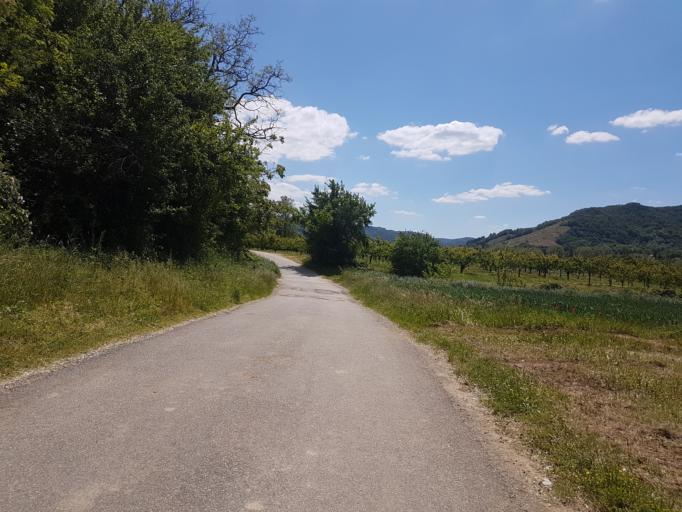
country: FR
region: Rhone-Alpes
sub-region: Departement de l'Ardeche
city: Saint-Jean-de-Muzols
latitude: 45.1025
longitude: 4.8215
